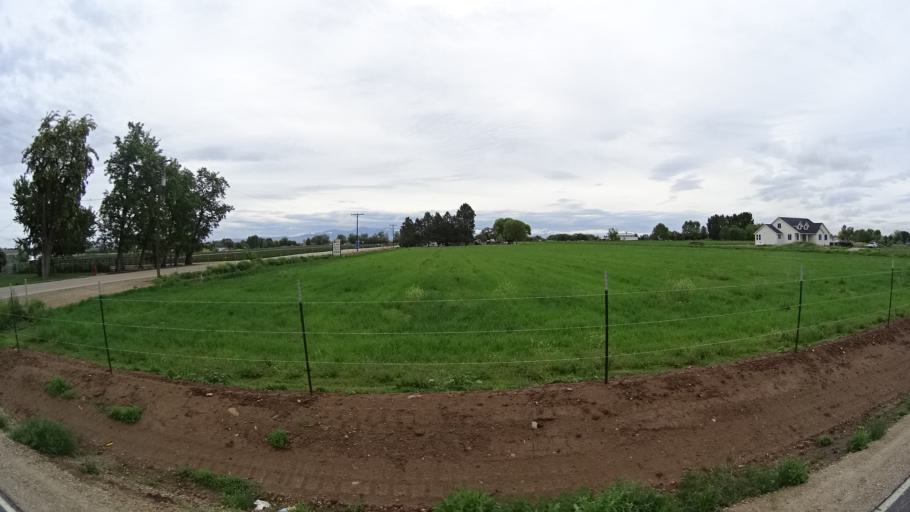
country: US
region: Idaho
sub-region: Ada County
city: Star
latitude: 43.7212
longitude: -116.4832
